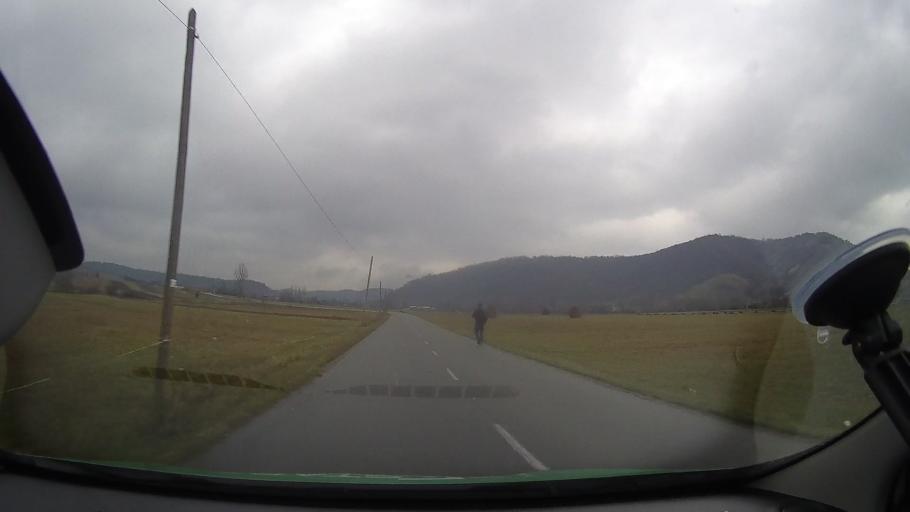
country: RO
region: Hunedoara
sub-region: Comuna Tomesti
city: Tomesti
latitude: 46.1911
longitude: 22.6314
